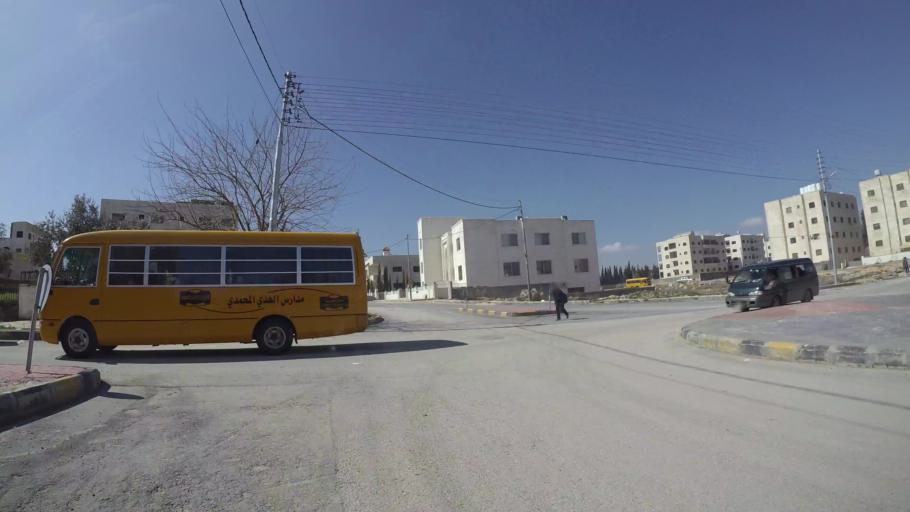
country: JO
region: Amman
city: Al Bunayyat ash Shamaliyah
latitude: 31.9035
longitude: 35.8957
